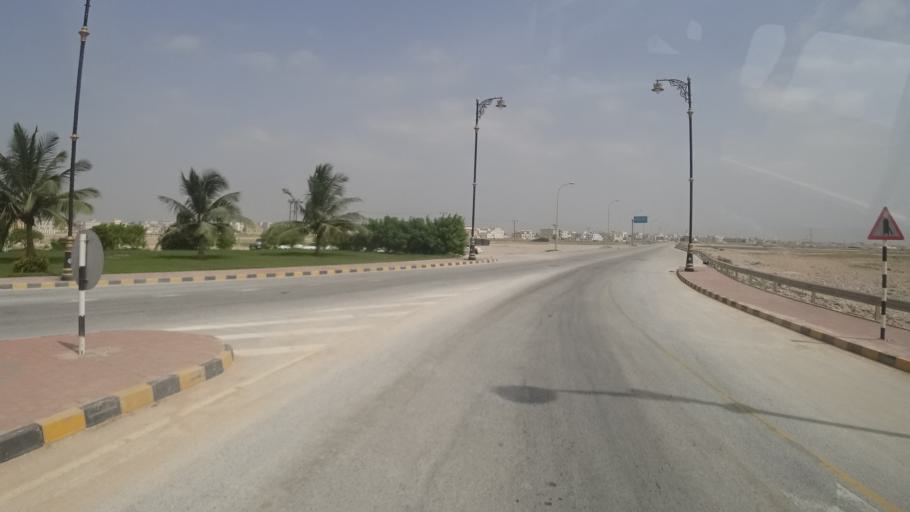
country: OM
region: Zufar
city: Salalah
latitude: 17.0524
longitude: 54.2187
